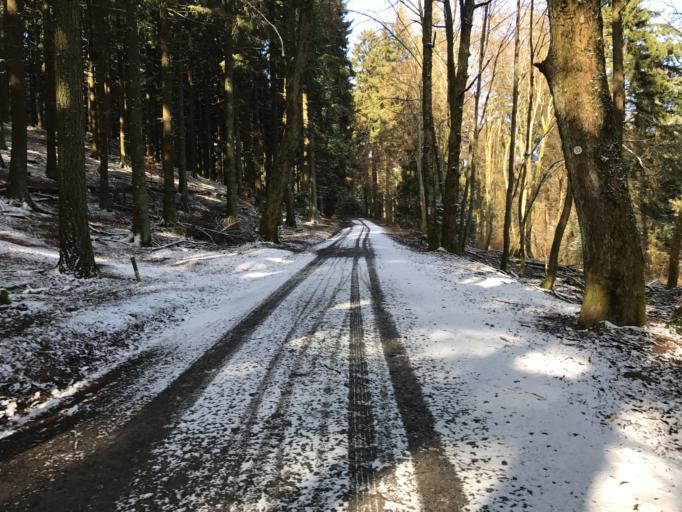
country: DE
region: Hesse
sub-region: Regierungsbezirk Darmstadt
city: Konigstein im Taunus
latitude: 50.2166
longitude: 8.4671
